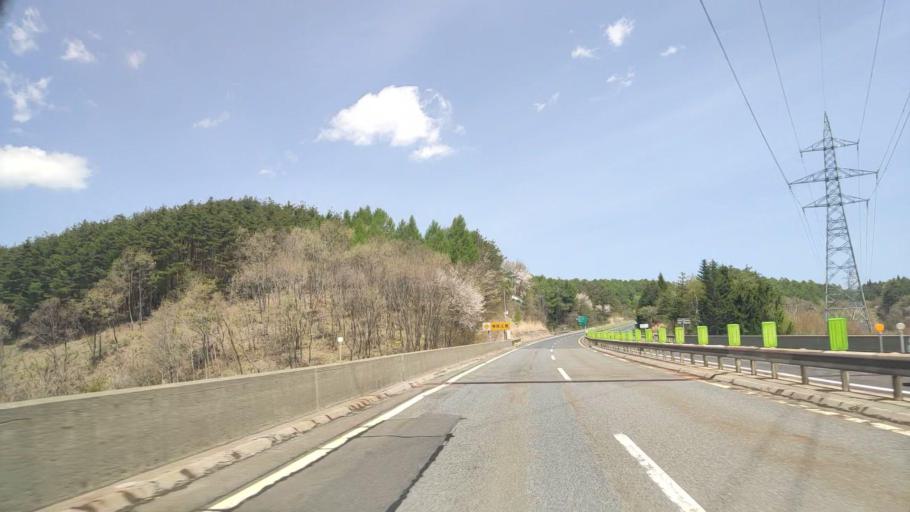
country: JP
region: Aomori
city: Hachinohe
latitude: 40.4235
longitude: 141.4391
